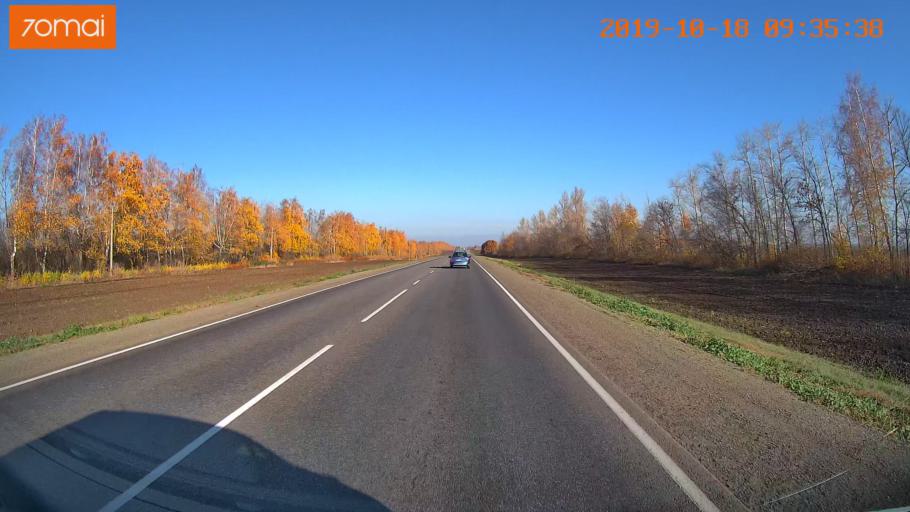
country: RU
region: Tula
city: Yefremov
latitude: 53.1950
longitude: 38.1479
